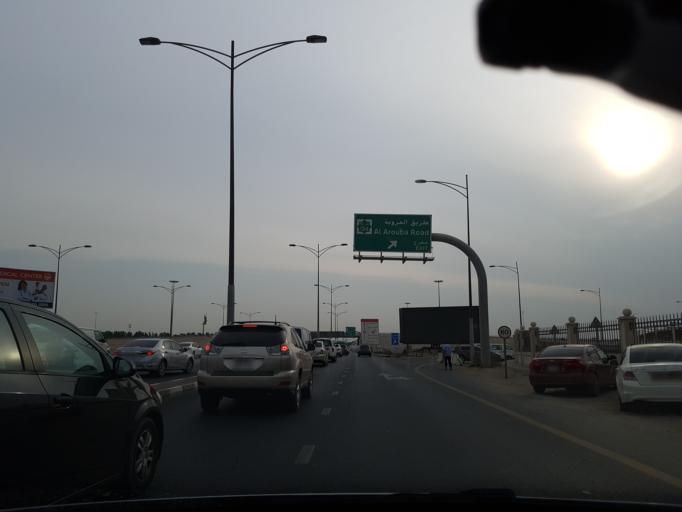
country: AE
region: Ajman
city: Ajman
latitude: 25.3754
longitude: 55.4569
